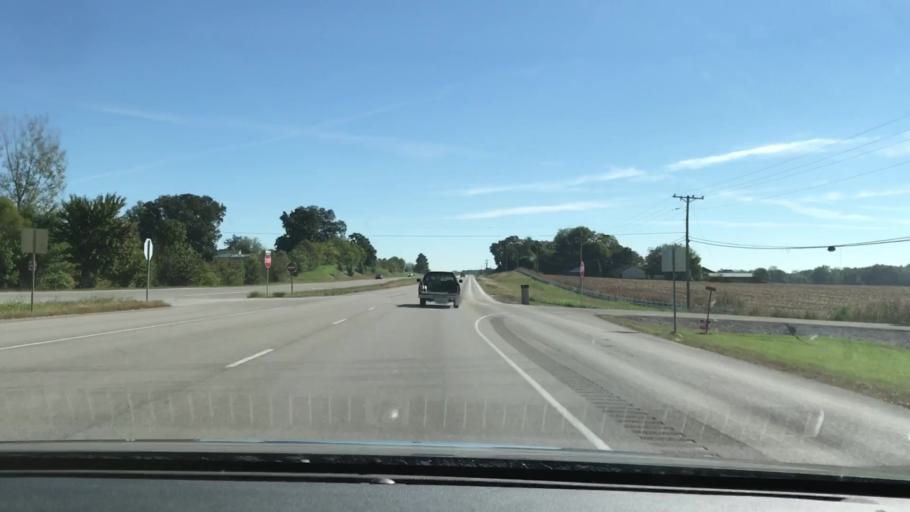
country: US
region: Kentucky
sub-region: Christian County
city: Hopkinsville
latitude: 36.8515
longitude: -87.3705
